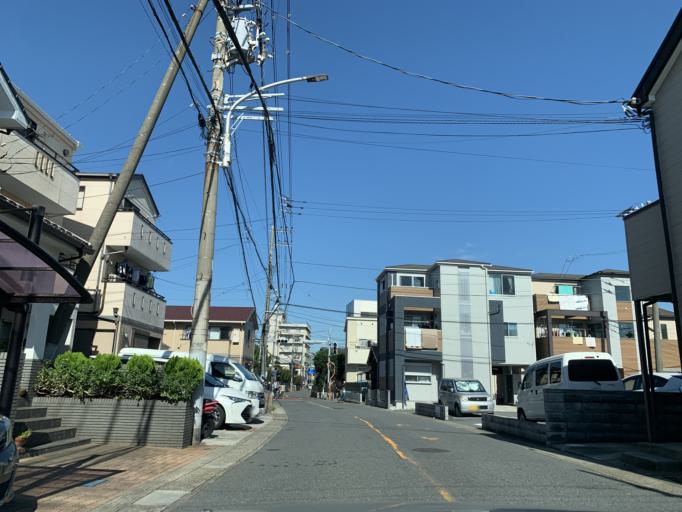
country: JP
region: Tokyo
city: Urayasu
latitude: 35.6768
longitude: 139.8931
